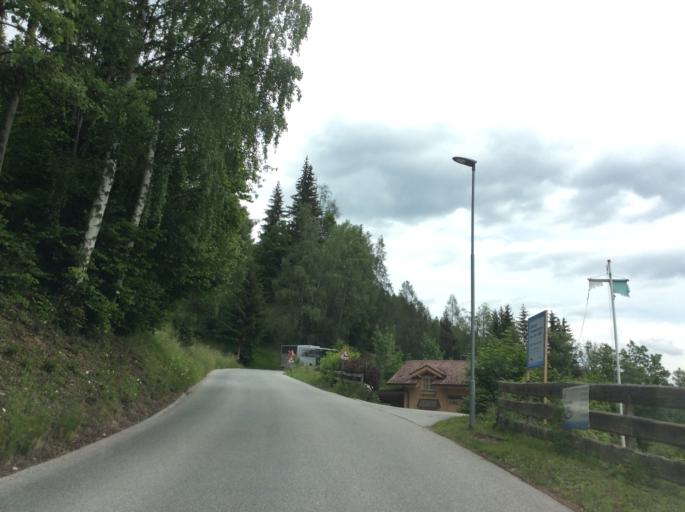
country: AT
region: Styria
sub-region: Politischer Bezirk Liezen
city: Schladming
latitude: 47.4030
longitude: 13.6935
